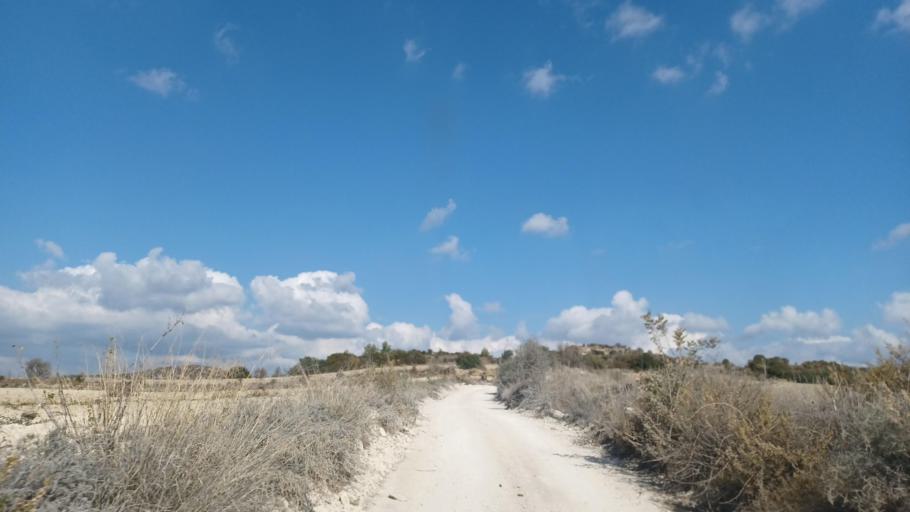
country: CY
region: Pafos
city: Mesogi
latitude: 34.8386
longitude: 32.5683
